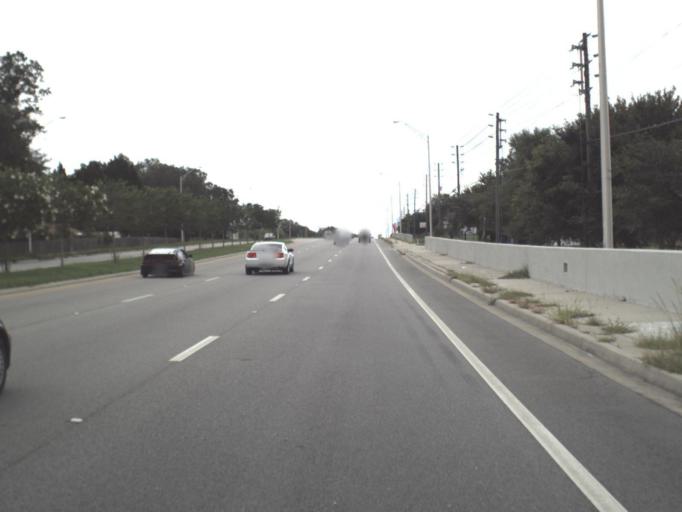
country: US
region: Florida
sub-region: Pasco County
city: Wesley Chapel
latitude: 28.2404
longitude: -82.3296
